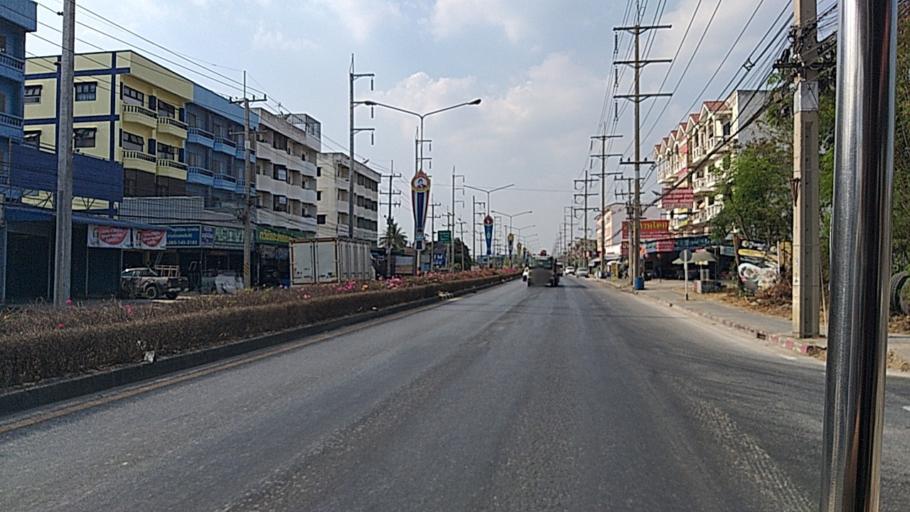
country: TH
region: Pathum Thani
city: Sam Khok
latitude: 14.0455
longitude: 100.5252
